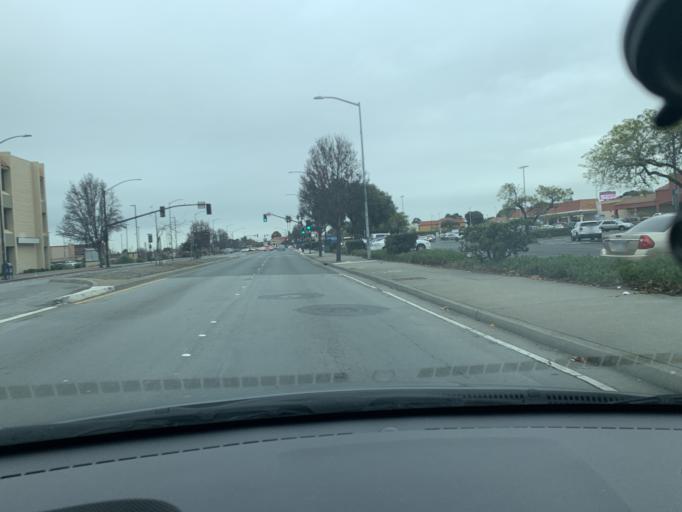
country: US
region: California
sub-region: Contra Costa County
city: Rollingwood
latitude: 37.9512
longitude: -122.3325
